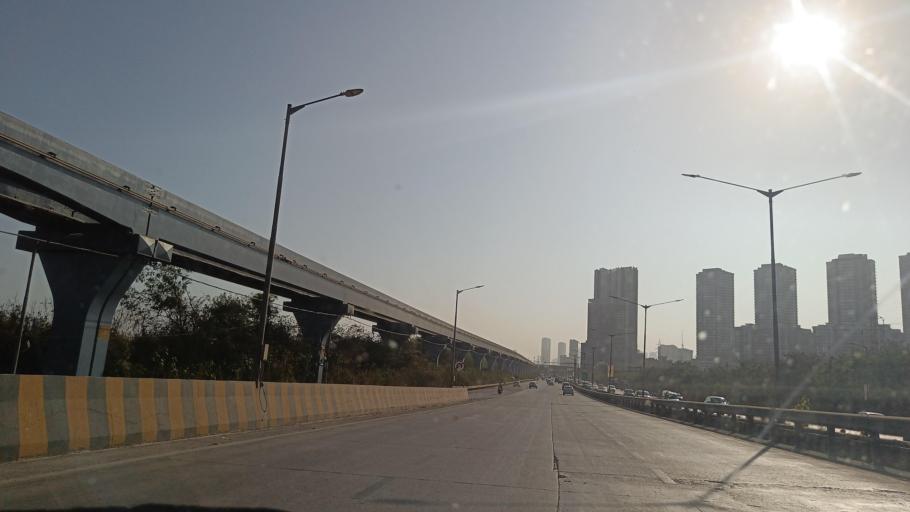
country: IN
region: Maharashtra
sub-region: Mumbai Suburban
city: Mumbai
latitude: 19.0281
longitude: 72.8864
